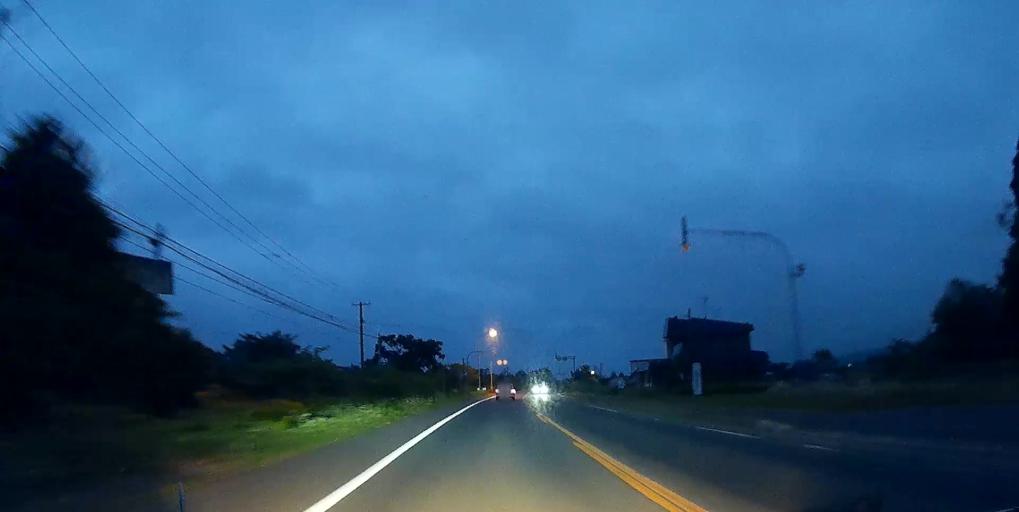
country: JP
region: Hokkaido
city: Nanae
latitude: 42.2217
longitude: 140.3709
